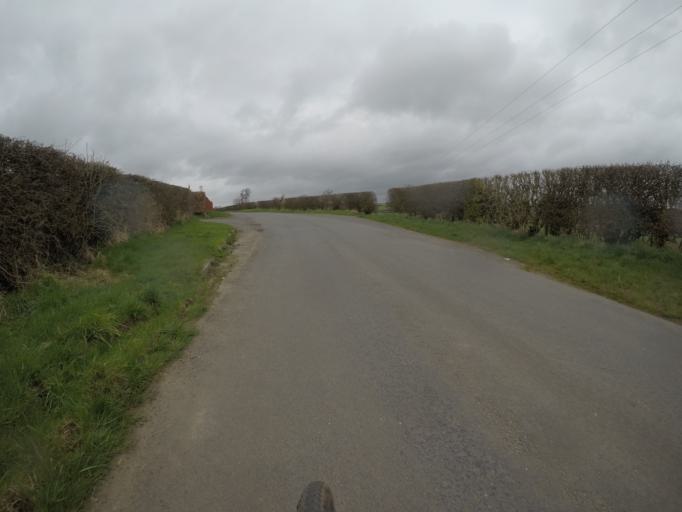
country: GB
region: Scotland
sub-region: East Ayrshire
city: Galston
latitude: 55.6176
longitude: -4.4348
